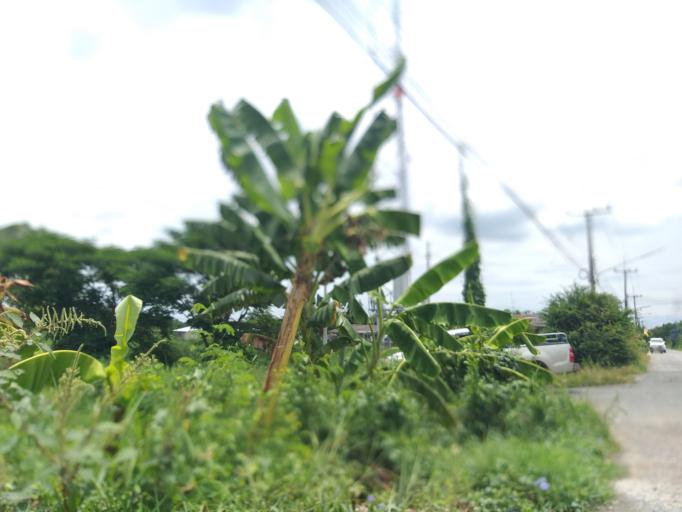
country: TH
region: Pathum Thani
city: Ban Lam Luk Ka
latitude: 13.9854
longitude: 100.8543
